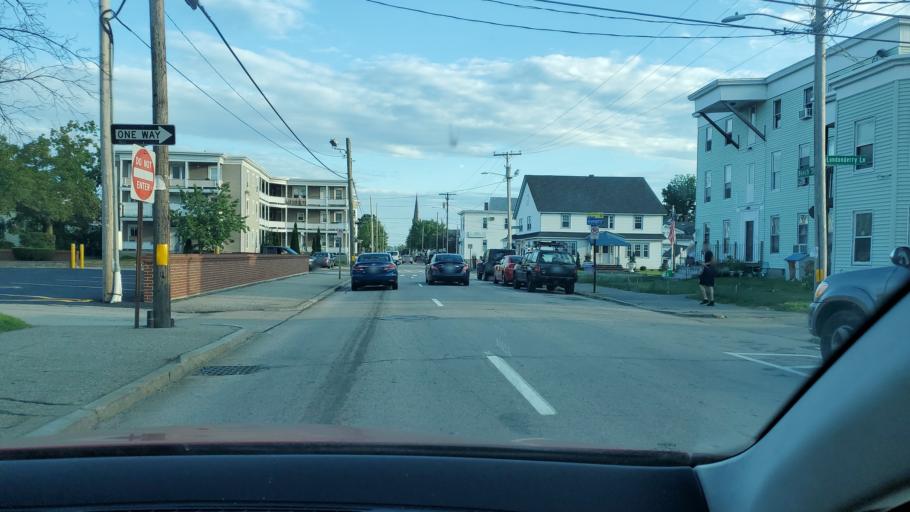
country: US
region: New Hampshire
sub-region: Hillsborough County
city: Manchester
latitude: 42.9907
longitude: -71.4553
